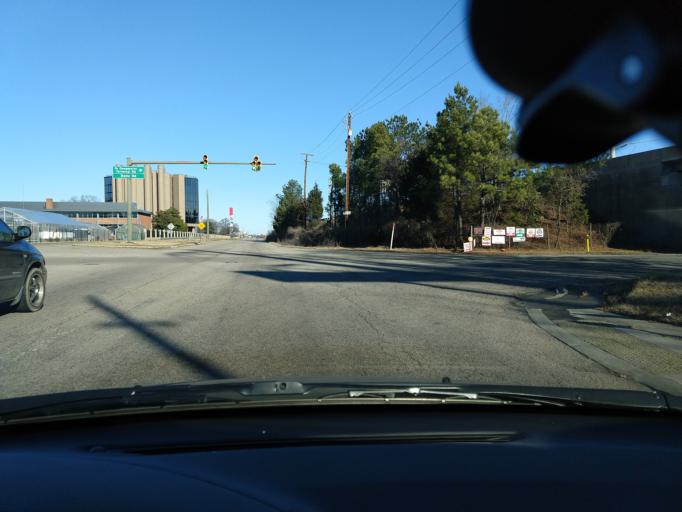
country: US
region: Virginia
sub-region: Chesterfield County
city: Bensley
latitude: 37.4680
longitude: -77.4283
